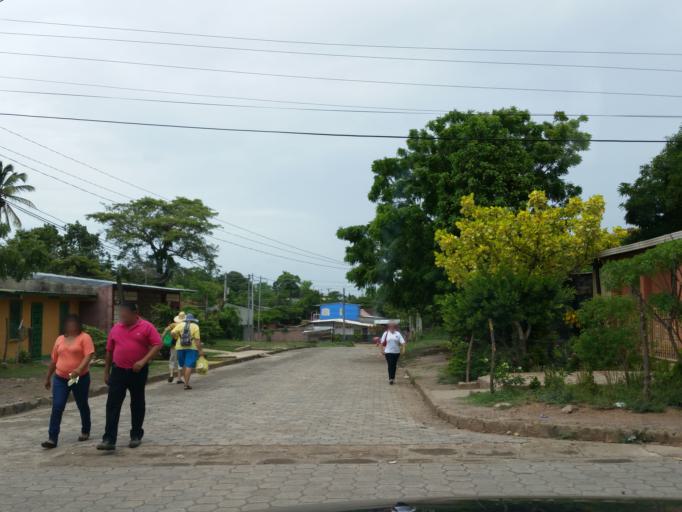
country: NI
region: Granada
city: Granada
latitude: 11.9353
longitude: -85.9592
